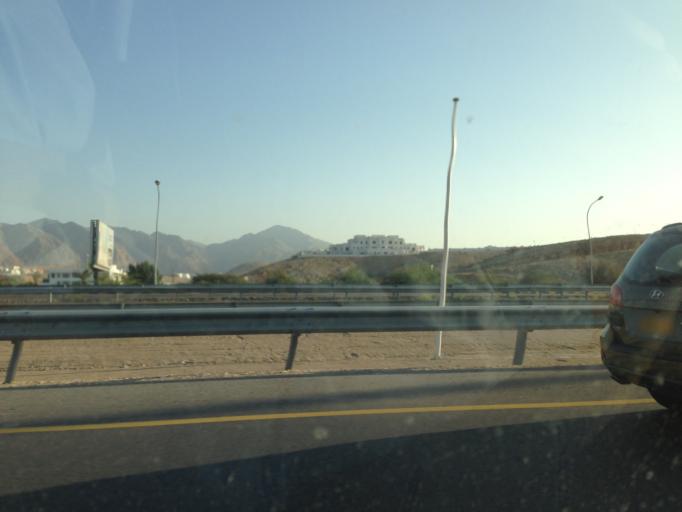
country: OM
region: Muhafazat Masqat
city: Bawshar
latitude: 23.5637
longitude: 58.3897
